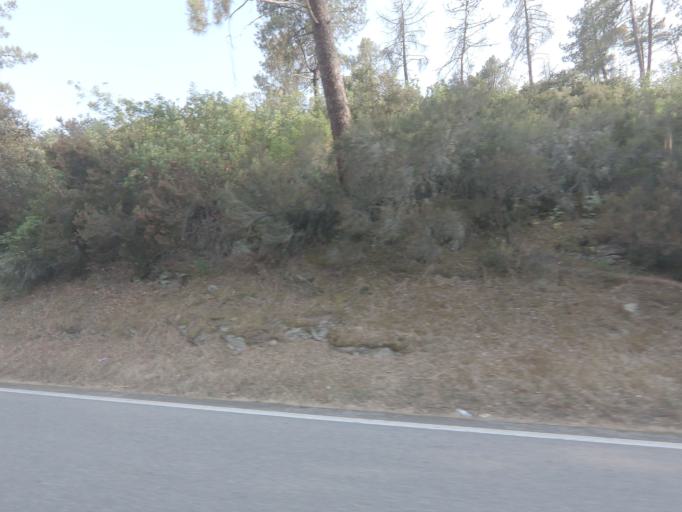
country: PT
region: Viseu
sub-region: Armamar
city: Armamar
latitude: 41.1591
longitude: -7.6472
